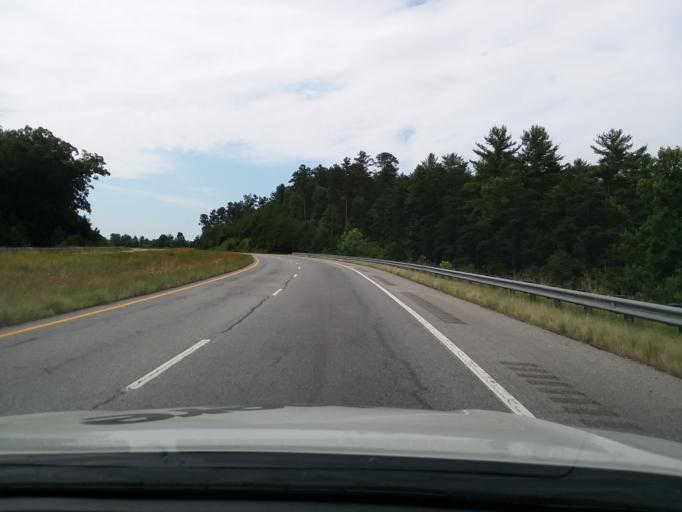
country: US
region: Georgia
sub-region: Rabun County
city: Clayton
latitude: 34.8044
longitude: -83.4265
